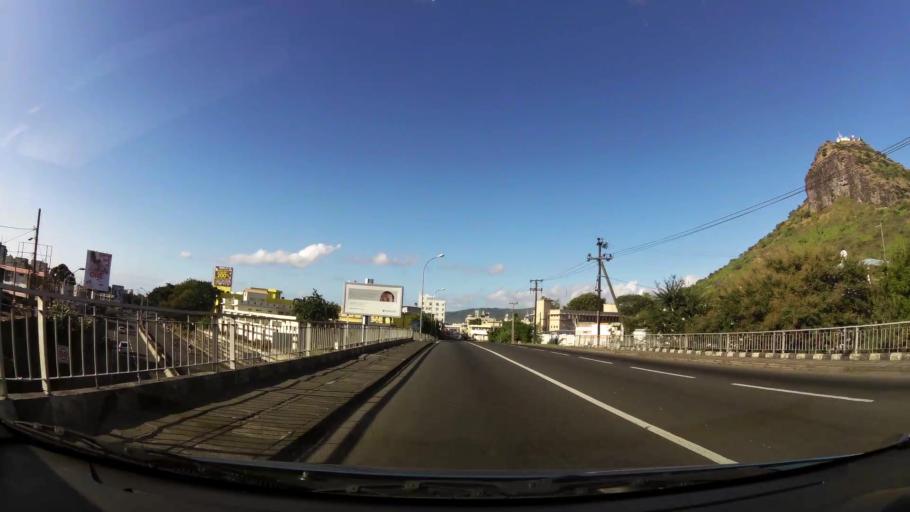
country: MU
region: Port Louis
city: Port Louis
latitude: -20.1682
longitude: 57.4849
